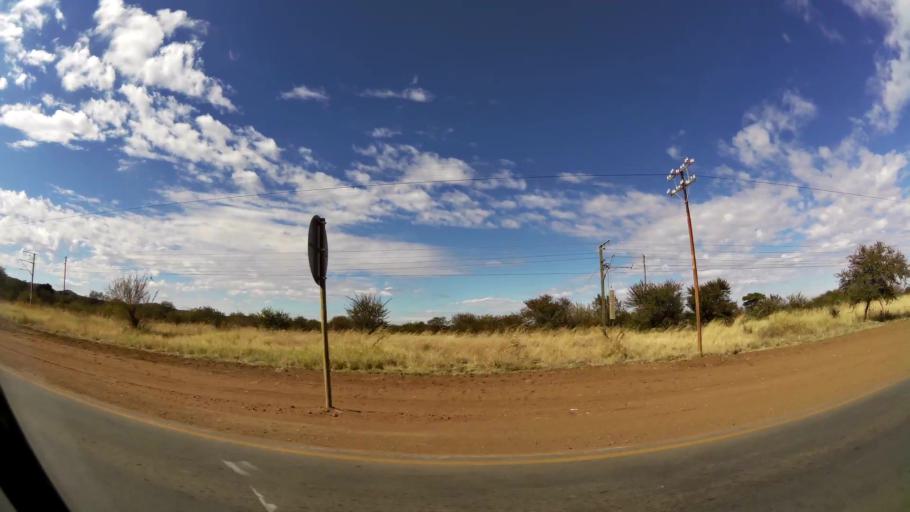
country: ZA
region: Limpopo
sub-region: Waterberg District Municipality
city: Bela-Bela
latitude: -24.8669
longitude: 28.3249
